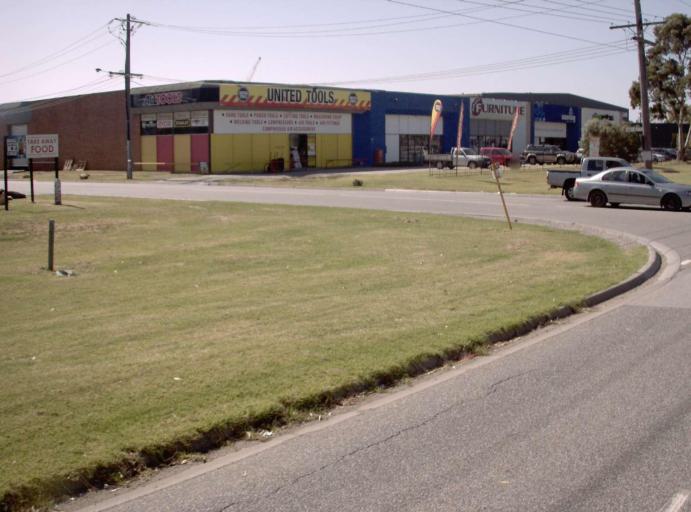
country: AU
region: Victoria
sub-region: Casey
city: Hampton Park
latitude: -38.0349
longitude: 145.2112
